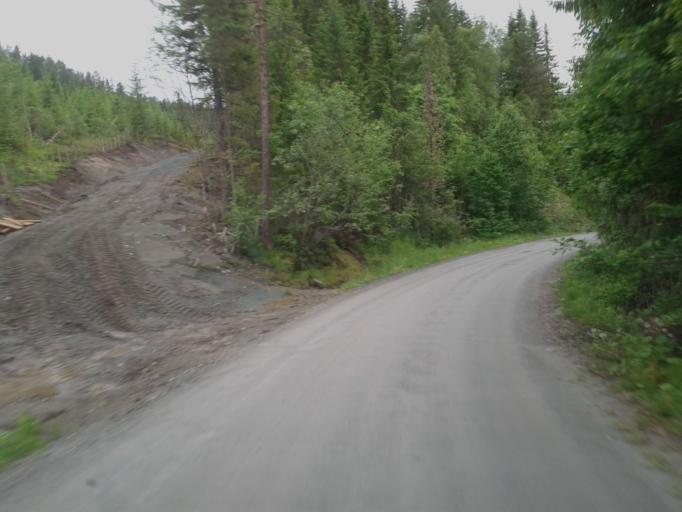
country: NO
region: Sor-Trondelag
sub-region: Melhus
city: Lundamo
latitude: 63.1312
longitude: 10.3253
